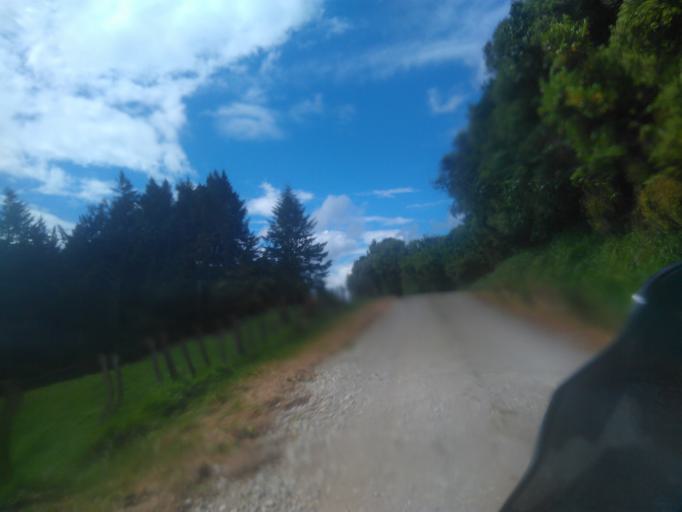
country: NZ
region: Hawke's Bay
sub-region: Wairoa District
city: Wairoa
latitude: -38.7746
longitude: 177.6370
